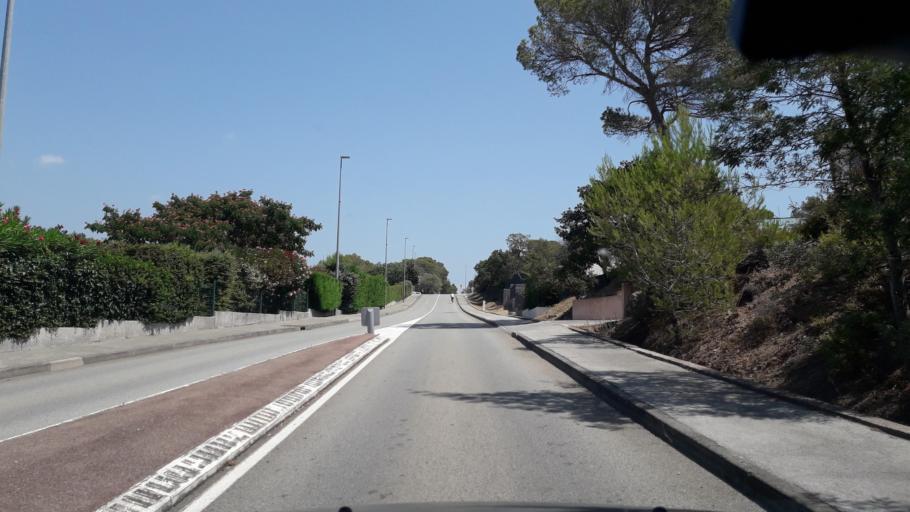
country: FR
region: Provence-Alpes-Cote d'Azur
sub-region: Departement du Var
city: Saint-Raphael
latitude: 43.4404
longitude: 6.7888
